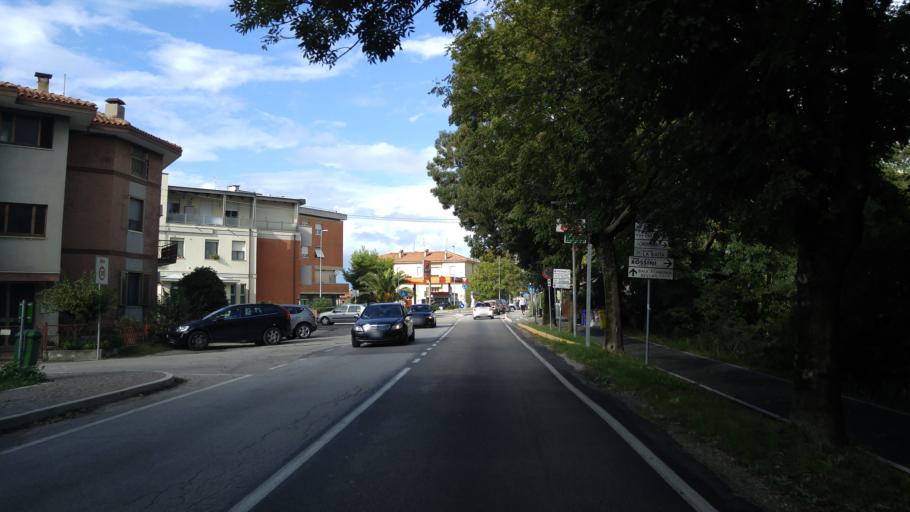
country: IT
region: The Marches
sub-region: Provincia di Pesaro e Urbino
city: Pesaro
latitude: 43.9153
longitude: 12.9027
